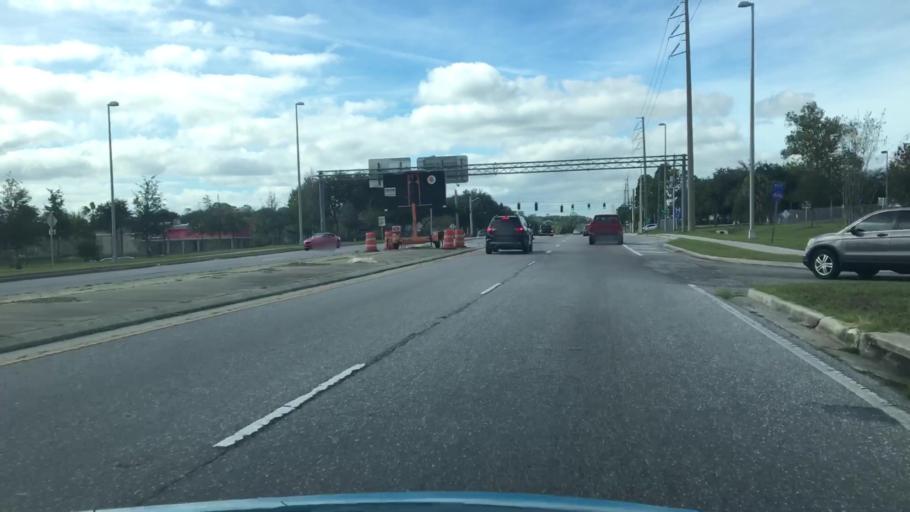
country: US
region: Florida
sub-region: Volusia County
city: Deltona
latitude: 28.9113
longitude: -81.2741
